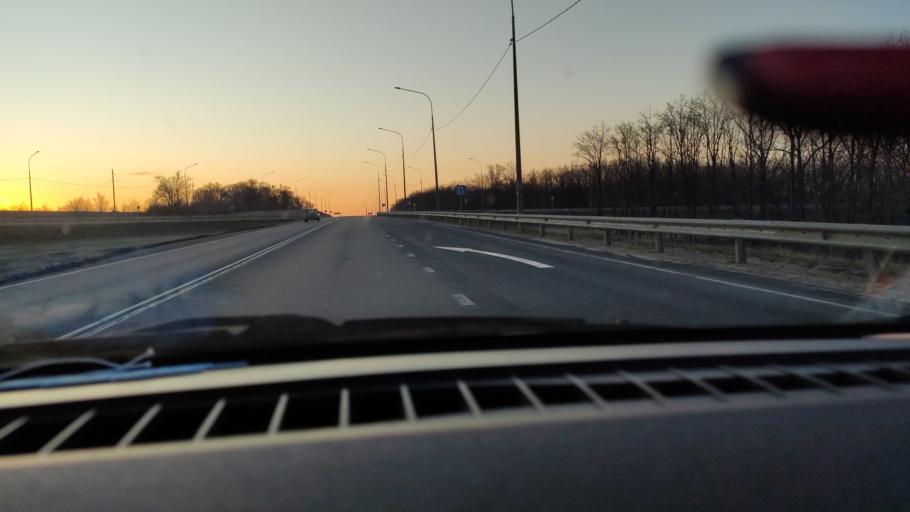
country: RU
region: Saratov
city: Yelshanka
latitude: 51.8250
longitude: 46.2961
